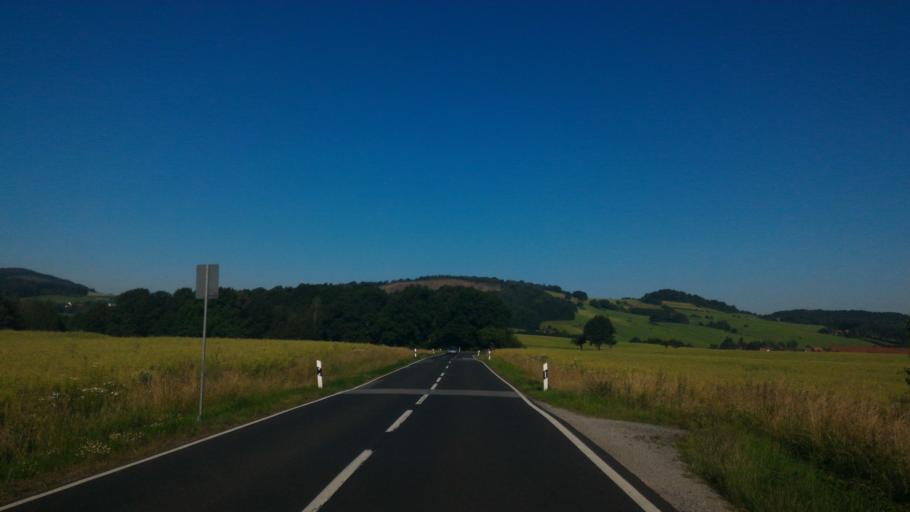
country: DE
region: Saxony
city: Mittelherwigsdorf
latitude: 50.9107
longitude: 14.7621
